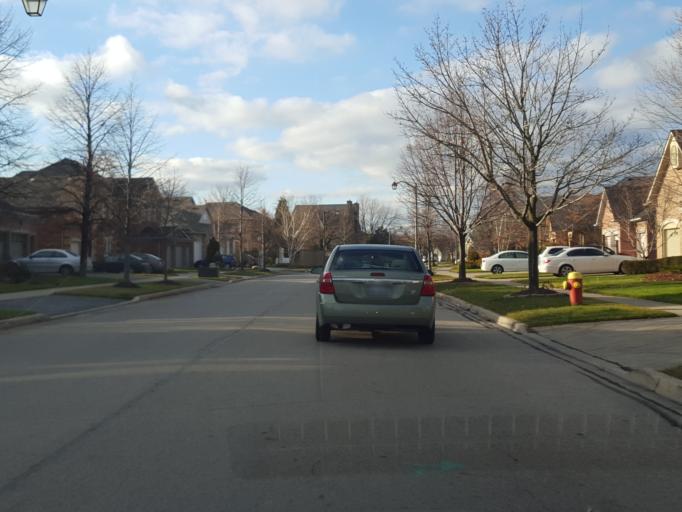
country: CA
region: Ontario
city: Burlington
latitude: 43.3894
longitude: -79.7991
